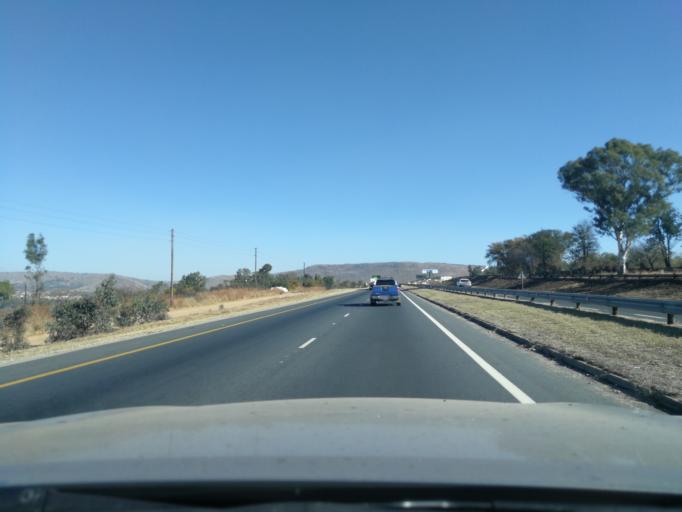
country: ZA
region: Gauteng
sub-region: West Rand District Municipality
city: Muldersdriseloop
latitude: -26.0473
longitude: 27.8407
